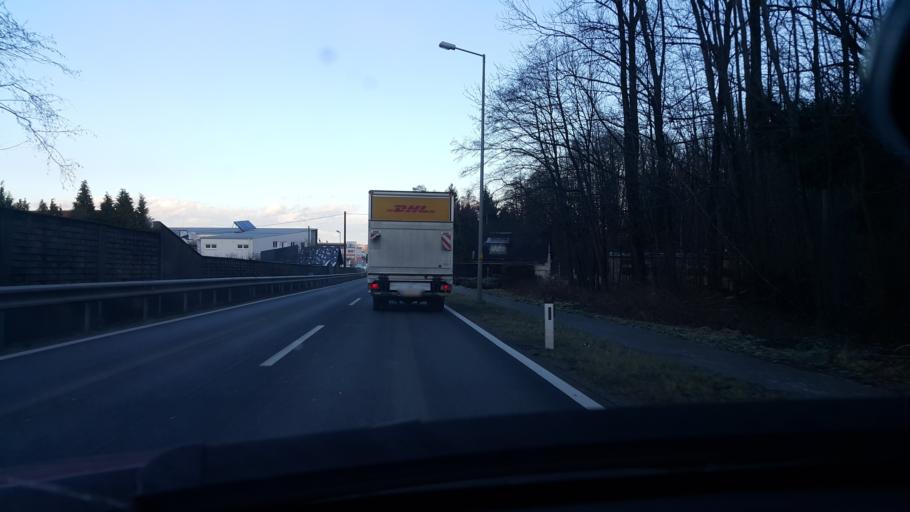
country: AT
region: Styria
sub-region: Politischer Bezirk Deutschlandsberg
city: Deutschlandsberg
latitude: 46.8138
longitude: 15.2316
